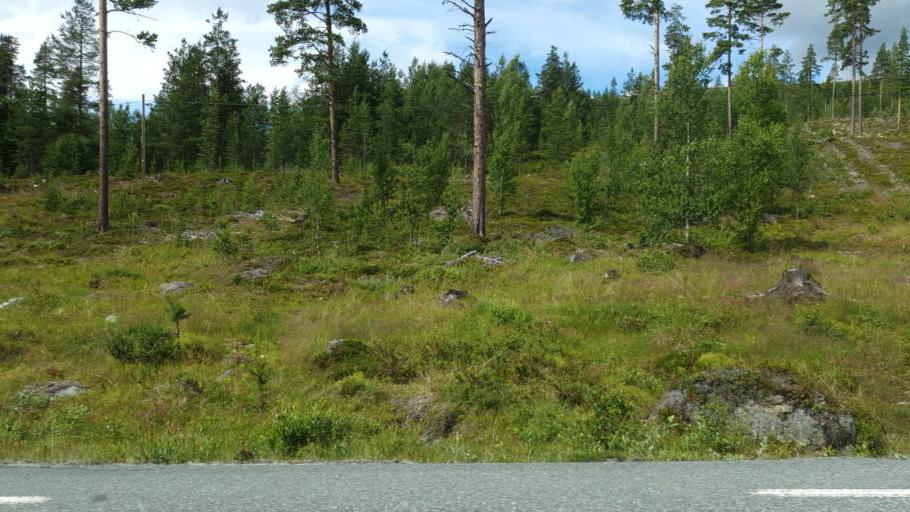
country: NO
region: Oppland
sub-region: Vaga
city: Vagamo
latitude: 61.7358
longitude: 9.0918
